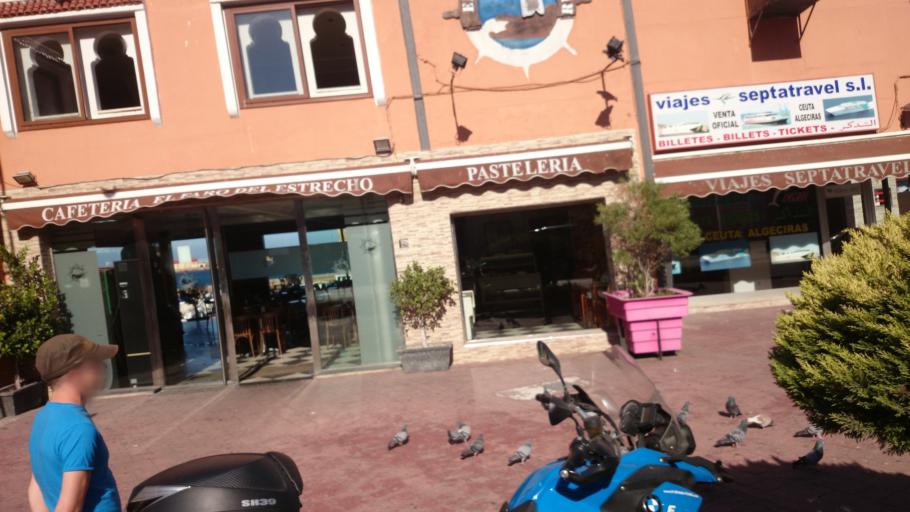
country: ES
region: Ceuta
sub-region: Ceuta
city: Ceuta
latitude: 35.8914
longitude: -5.3191
